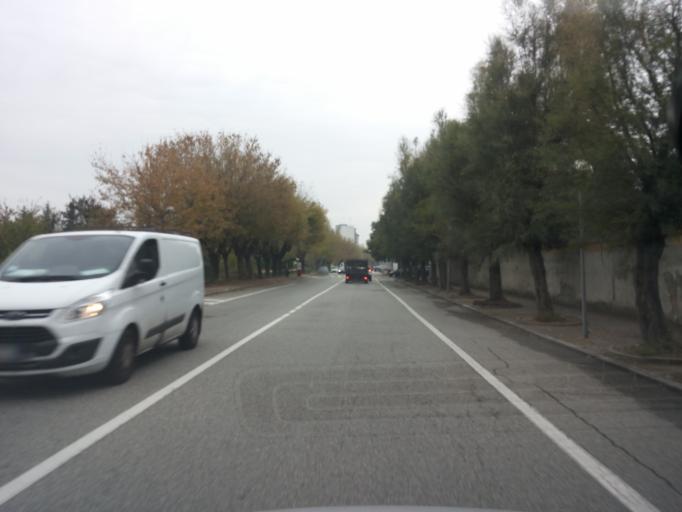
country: IT
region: Piedmont
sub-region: Provincia di Vercelli
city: Vercelli
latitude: 45.3105
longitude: 8.4250
